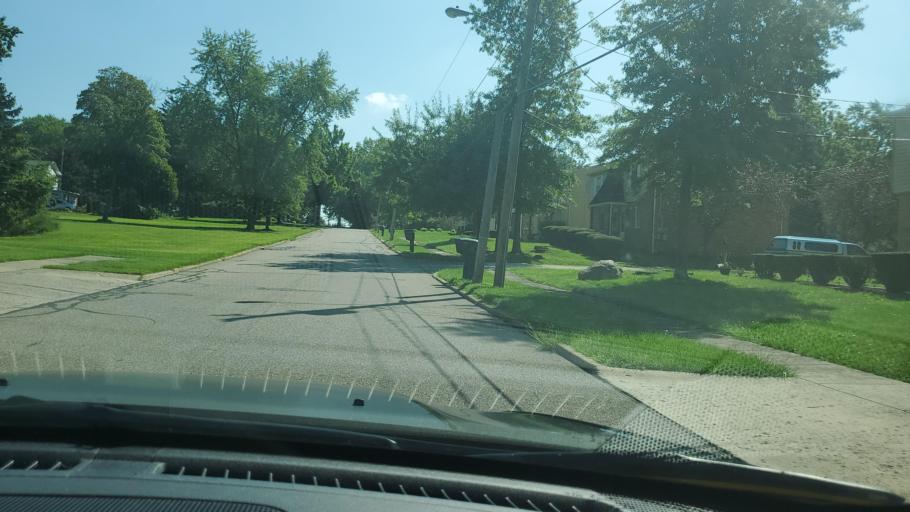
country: US
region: Ohio
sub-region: Trumbull County
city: Girard
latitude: 41.1671
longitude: -80.6911
